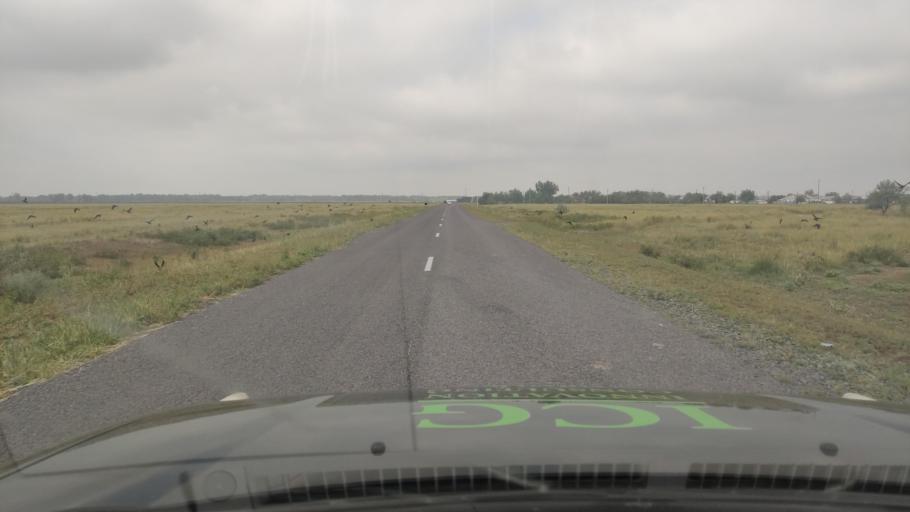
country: KZ
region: Pavlodar
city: Aksu
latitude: 51.9369
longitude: 77.3073
